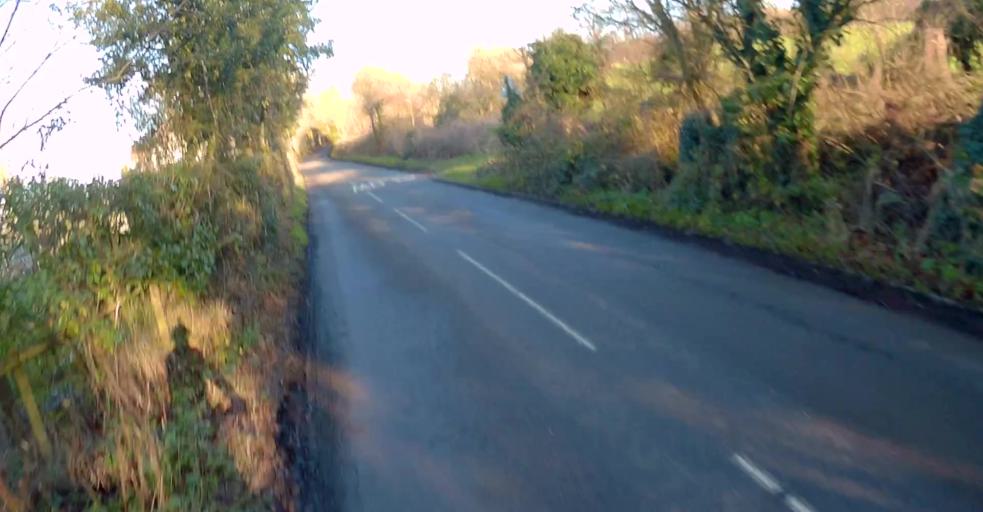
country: GB
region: England
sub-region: Hampshire
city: Old Basing
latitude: 51.2832
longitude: -1.0025
